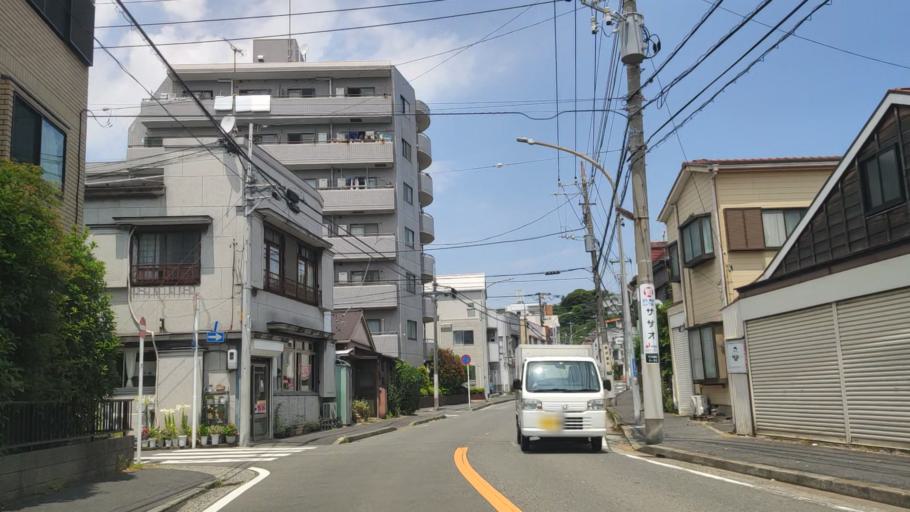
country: JP
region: Kanagawa
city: Yokohama
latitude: 35.4331
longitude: 139.6572
